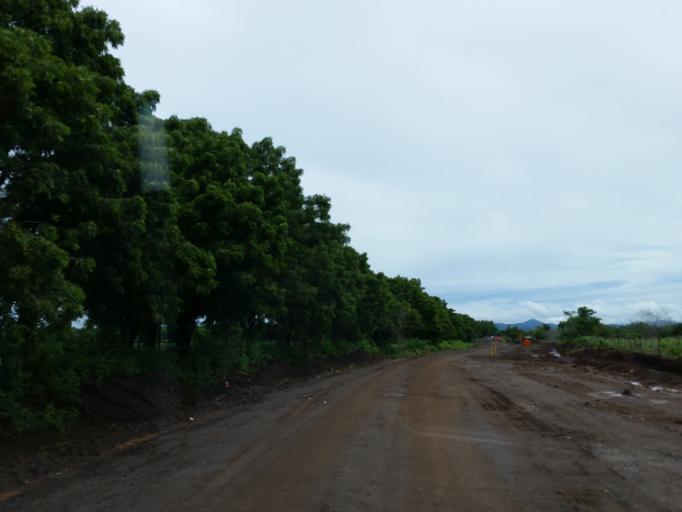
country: NI
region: Leon
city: Larreynaga
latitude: 12.5564
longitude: -86.6225
